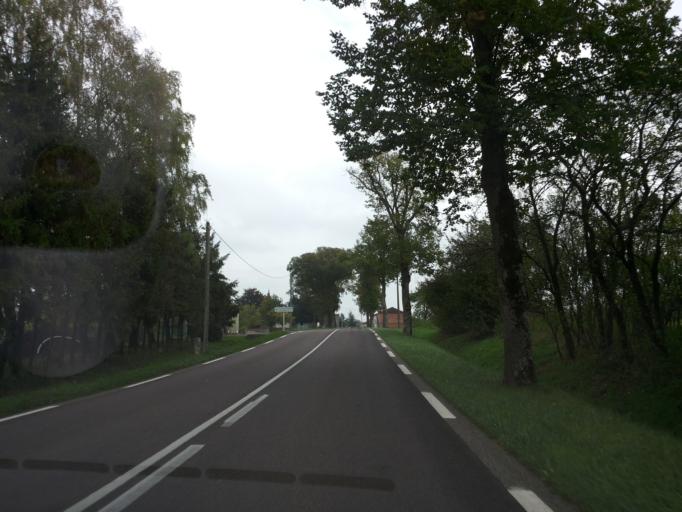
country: FR
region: Lorraine
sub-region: Departement de la Moselle
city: Dieuze
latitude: 48.7173
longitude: 6.7666
